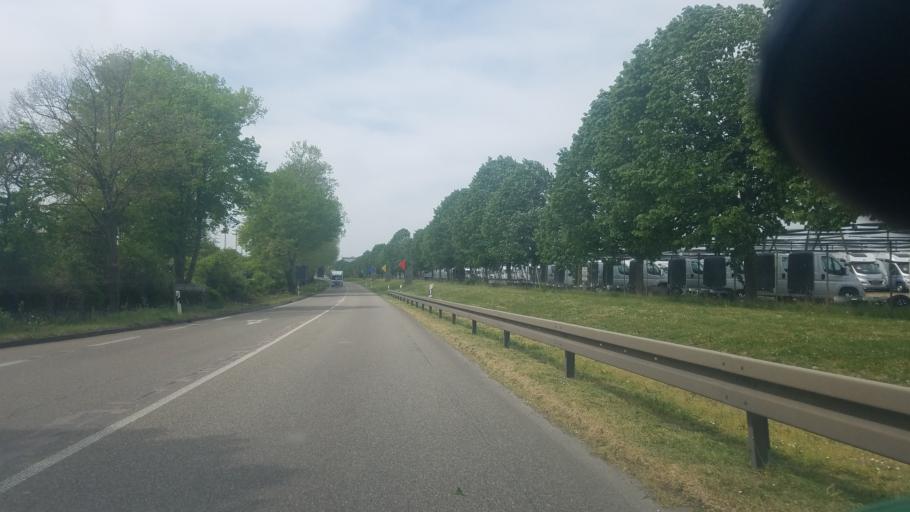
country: DE
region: Baden-Wuerttemberg
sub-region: Freiburg Region
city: Kehl
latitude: 48.5811
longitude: 7.8191
